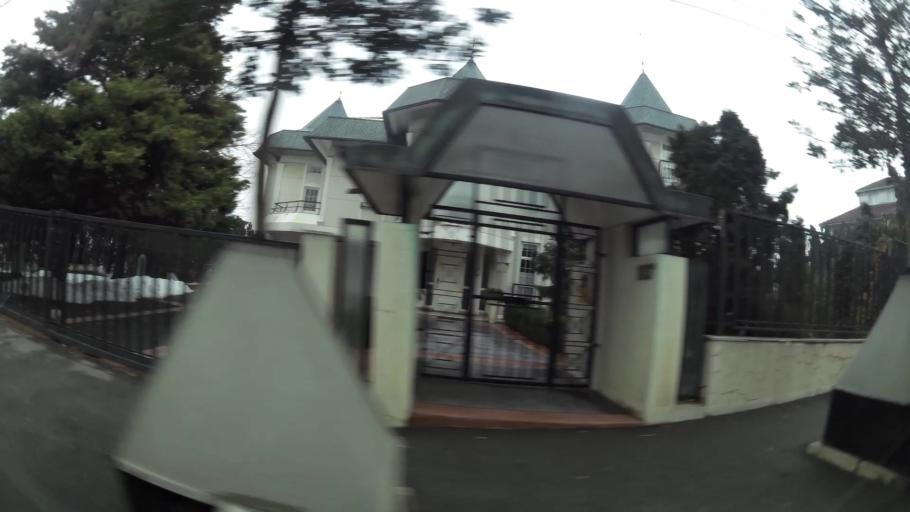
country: RS
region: Central Serbia
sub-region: Belgrade
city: Zvezdara
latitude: 44.7695
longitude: 20.5131
